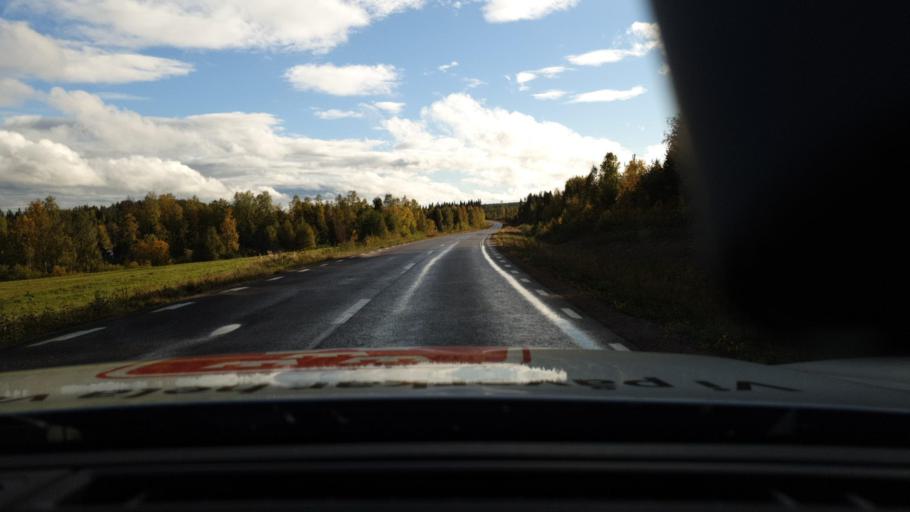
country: SE
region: Norrbotten
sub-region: Overkalix Kommun
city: OEverkalix
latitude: 66.7627
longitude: 22.6821
